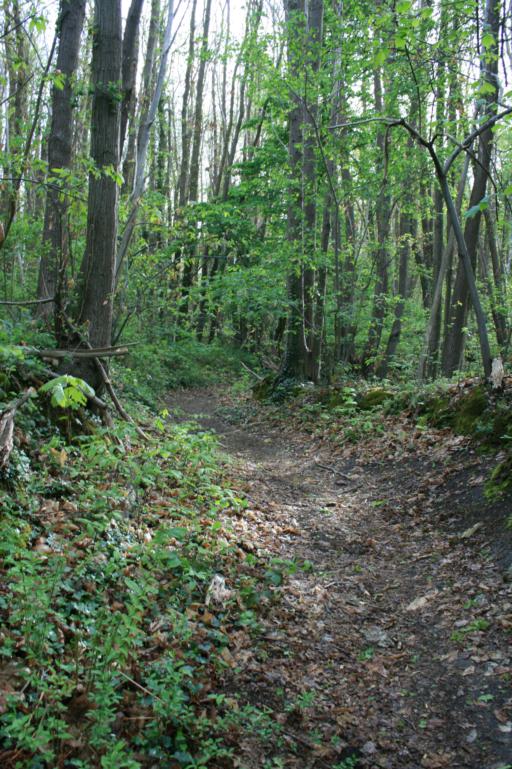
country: FR
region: Ile-de-France
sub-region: Departement des Yvelines
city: Vaux-sur-Seine
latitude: 49.0019
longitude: 1.9821
